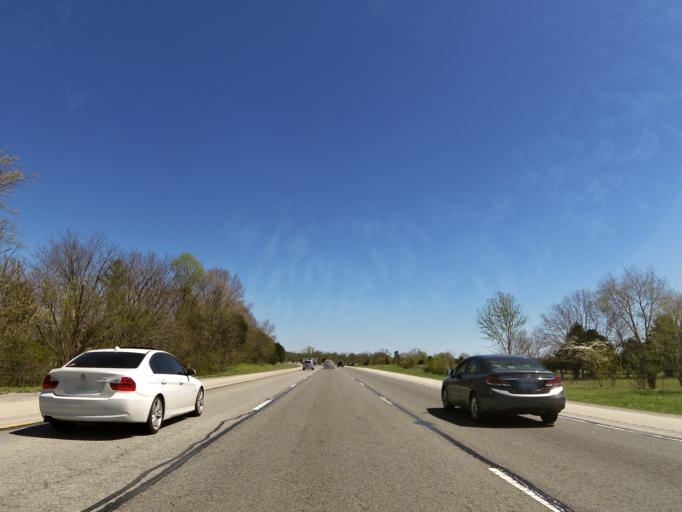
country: US
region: Kentucky
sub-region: Warren County
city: Bowling Green
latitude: 37.0122
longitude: -86.2975
